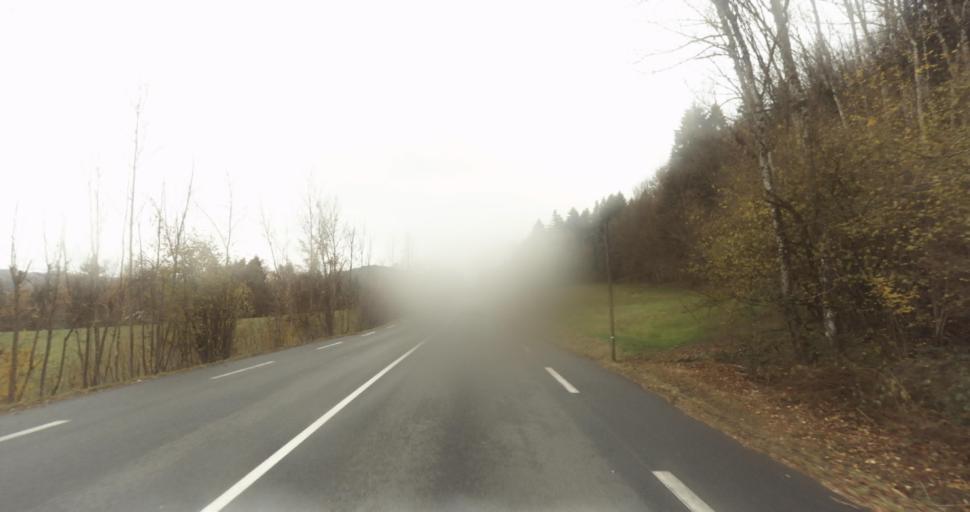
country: FR
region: Rhone-Alpes
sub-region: Departement de la Haute-Savoie
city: Evires
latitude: 46.0127
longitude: 6.2100
